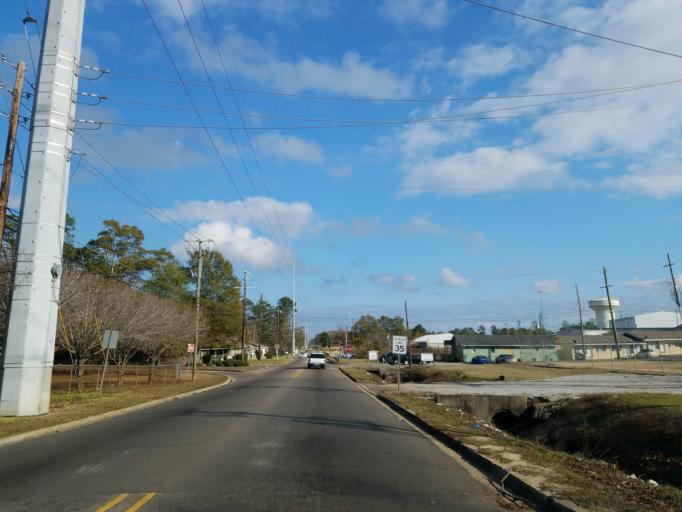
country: US
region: Mississippi
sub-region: Lamar County
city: Arnold Line
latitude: 31.3357
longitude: -89.3363
